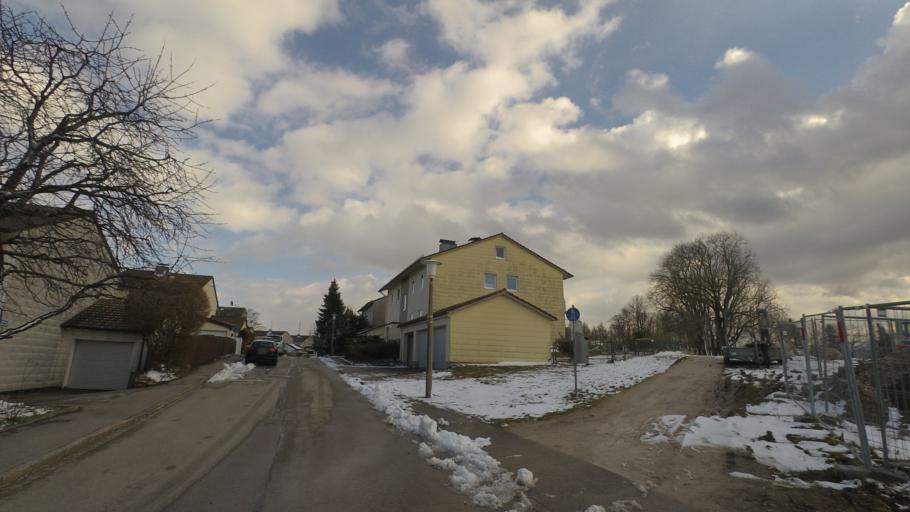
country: DE
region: Bavaria
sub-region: Upper Bavaria
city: Traunstein
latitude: 47.8761
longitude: 12.6282
